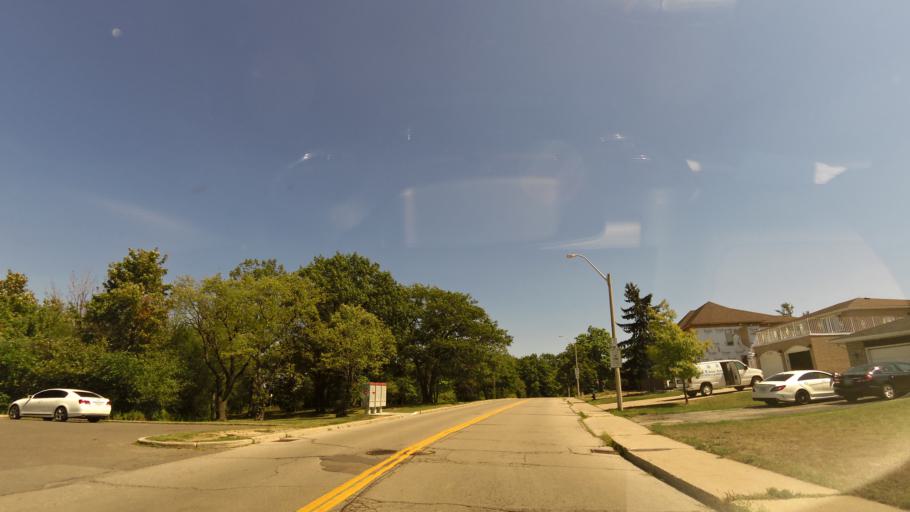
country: CA
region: Ontario
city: Ancaster
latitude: 43.2454
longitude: -79.9308
